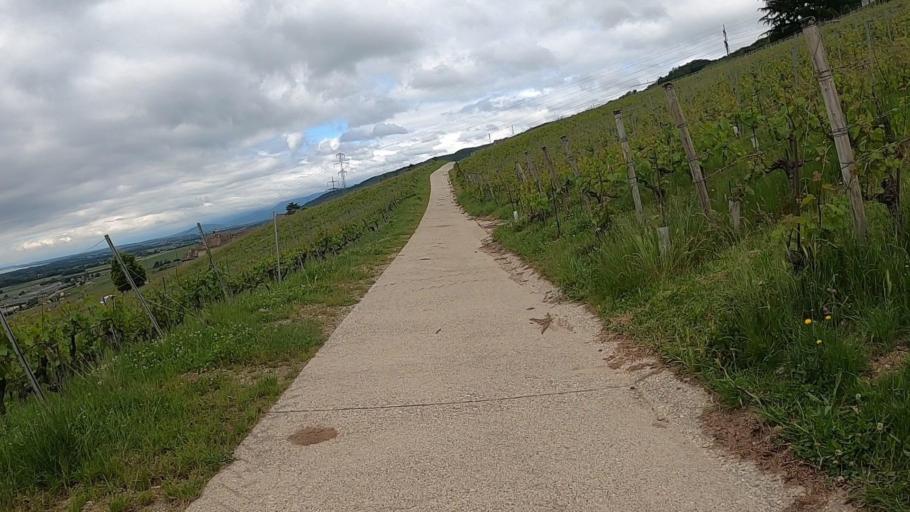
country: CH
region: Vaud
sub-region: Nyon District
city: Rolle
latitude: 46.4739
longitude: 6.3343
